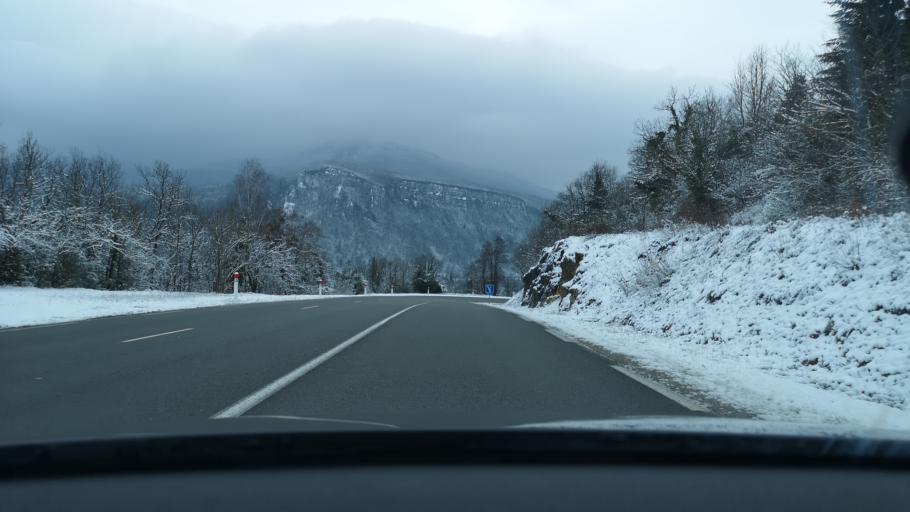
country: FR
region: Franche-Comte
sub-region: Departement du Jura
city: Moirans-en-Montagne
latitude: 46.3761
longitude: 5.7086
